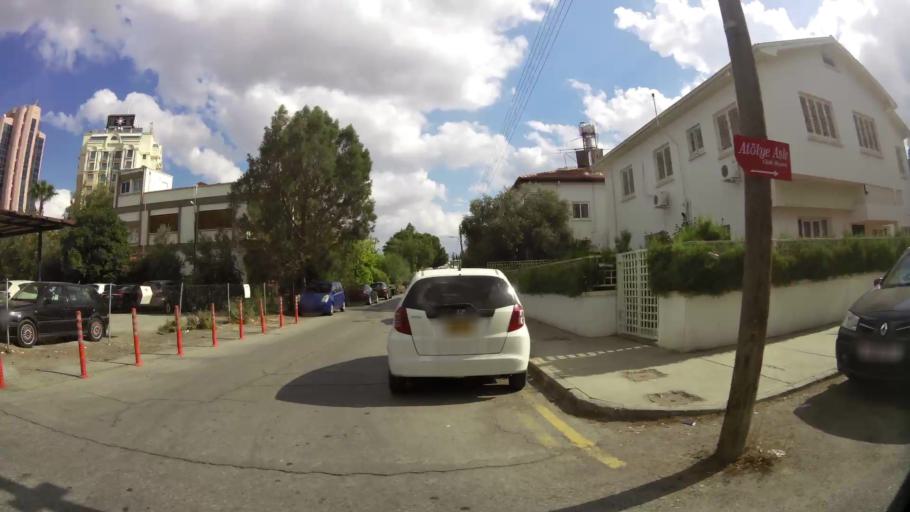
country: CY
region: Lefkosia
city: Nicosia
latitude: 35.1904
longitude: 33.3507
